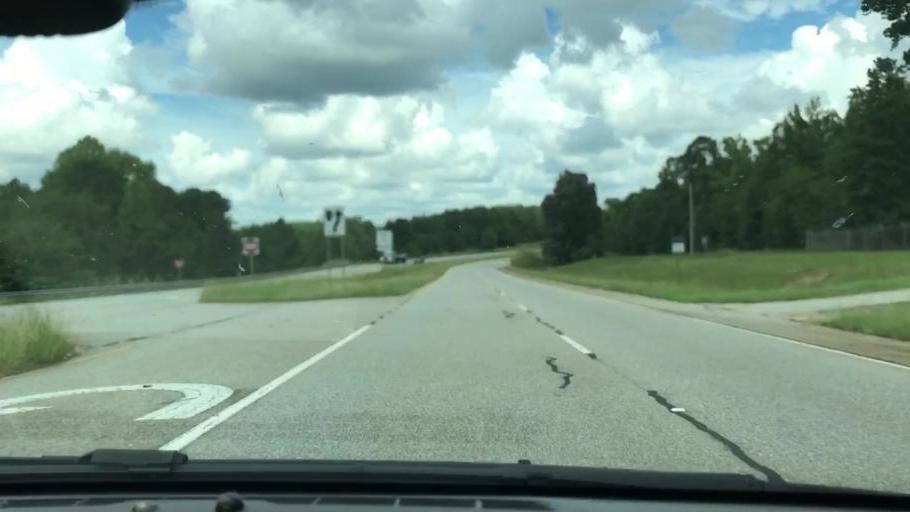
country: US
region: Georgia
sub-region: Stewart County
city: Lumpkin
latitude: 32.0874
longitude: -84.8073
